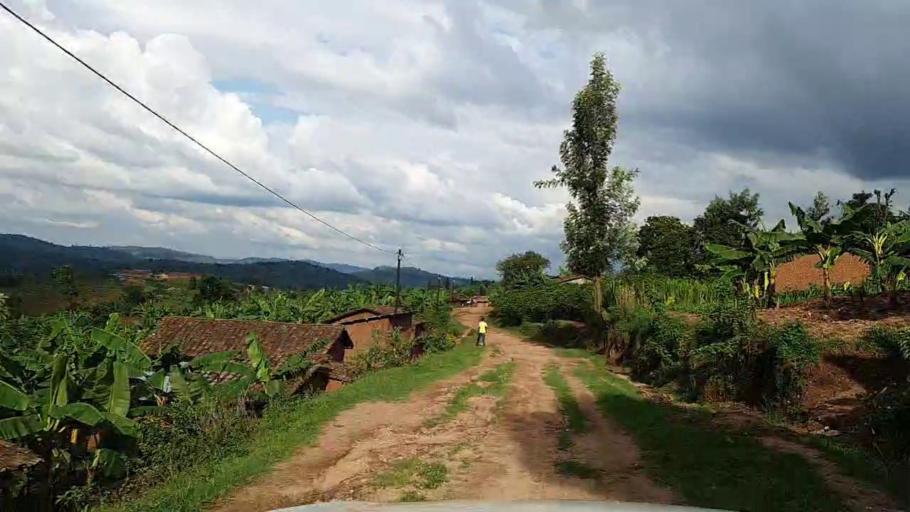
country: RW
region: Southern Province
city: Gikongoro
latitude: -2.4244
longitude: 29.6431
